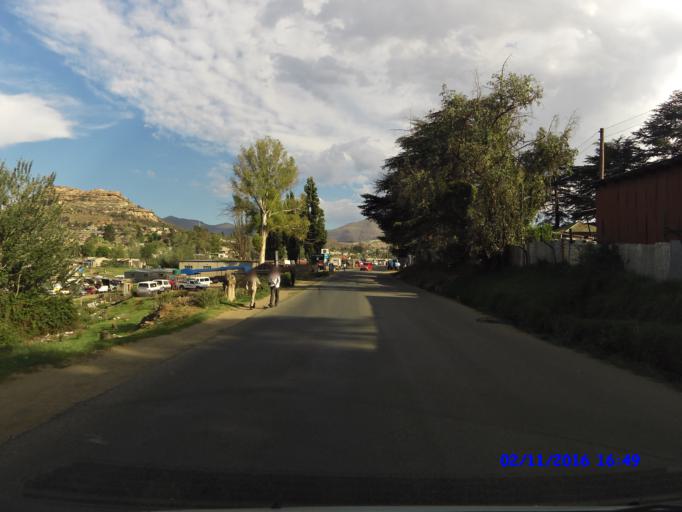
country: LS
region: Butha-Buthe
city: Butha-Buthe
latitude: -28.7637
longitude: 28.2508
